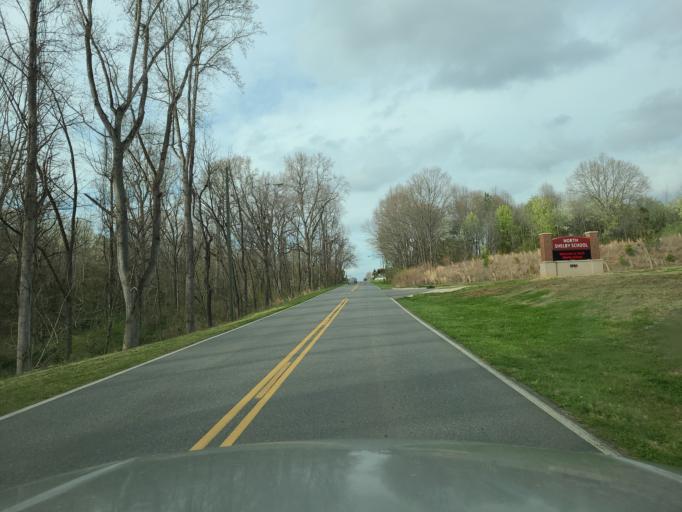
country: US
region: North Carolina
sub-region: Cleveland County
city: Shelby
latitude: 35.2663
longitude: -81.5708
